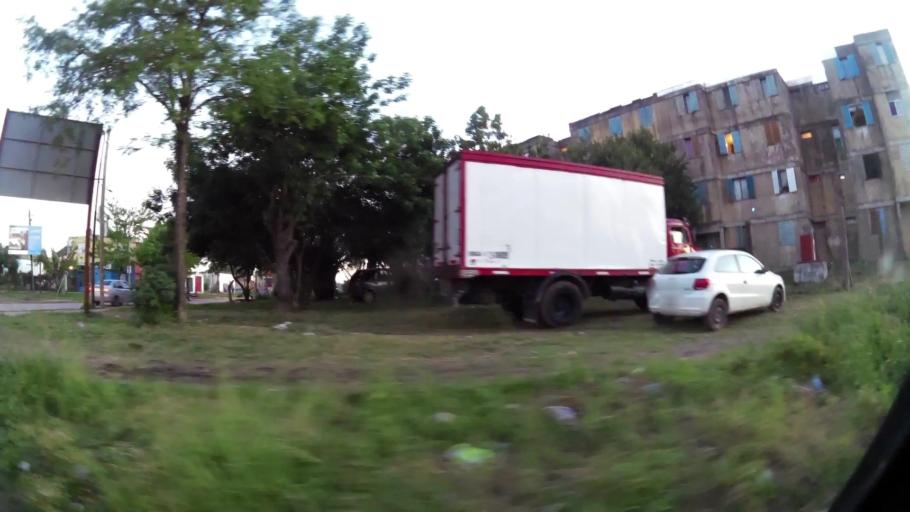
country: AR
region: Buenos Aires
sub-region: Partido de Almirante Brown
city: Adrogue
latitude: -34.7892
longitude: -58.3230
